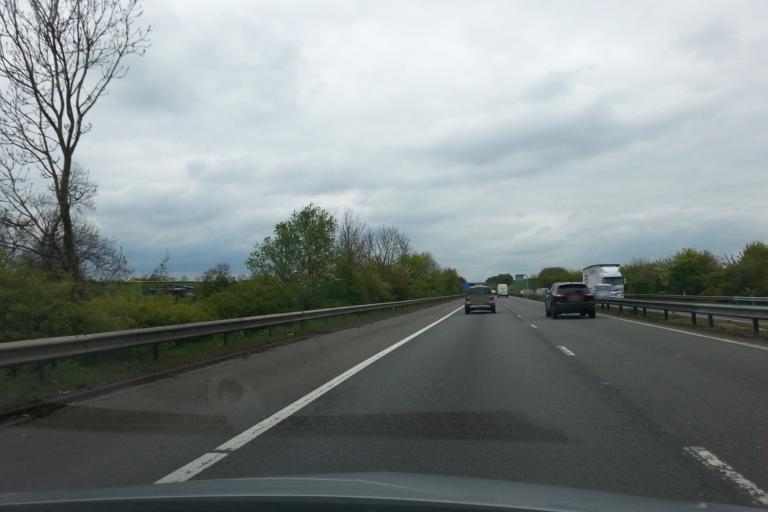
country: GB
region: England
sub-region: Derbyshire
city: Netherseal
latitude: 52.6660
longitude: -1.5698
